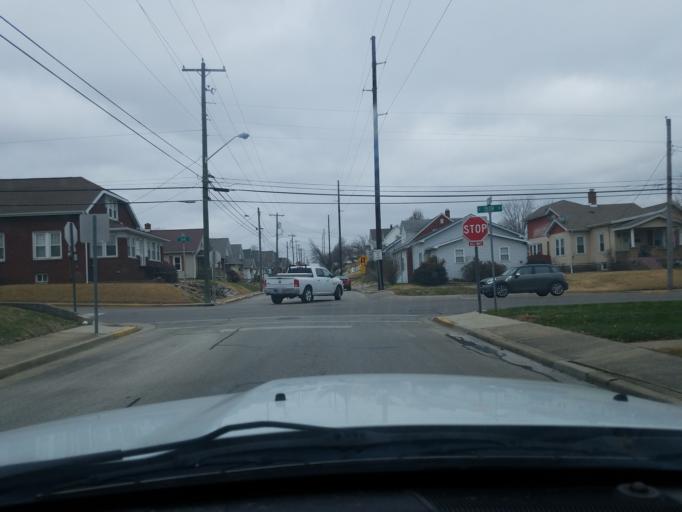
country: US
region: Indiana
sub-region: Dubois County
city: Jasper
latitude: 38.4001
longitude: -86.9286
